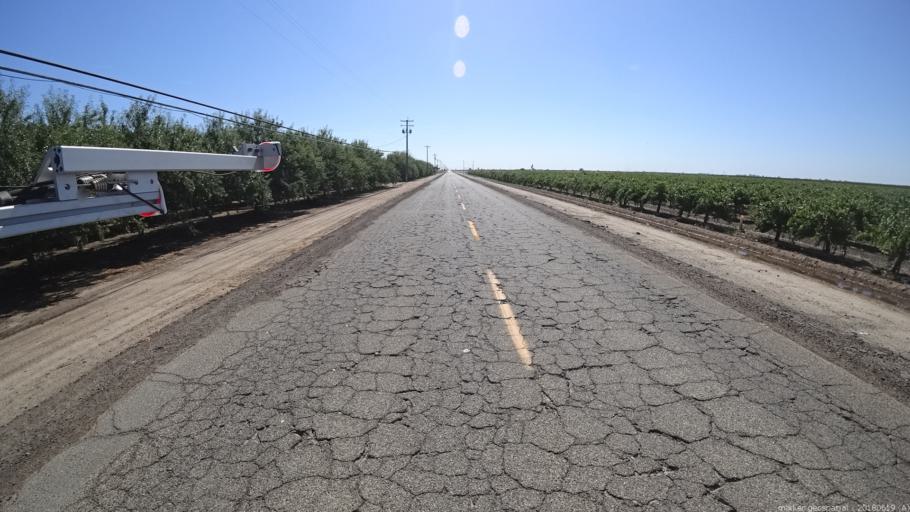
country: US
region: California
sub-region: Fresno County
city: Biola
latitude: 36.8367
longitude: -120.1449
